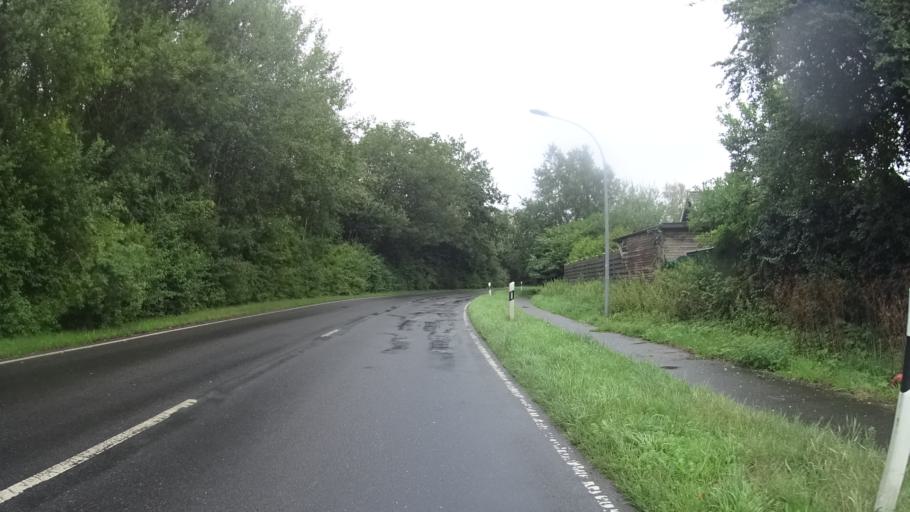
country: DE
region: Schleswig-Holstein
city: Alveslohe
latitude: 53.7883
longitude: 9.9213
